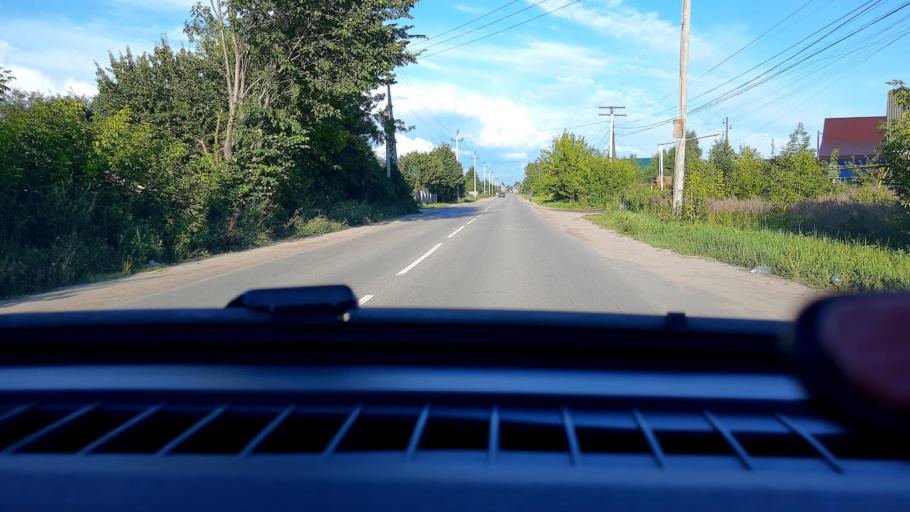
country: RU
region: Nizjnij Novgorod
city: Bor
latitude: 56.3539
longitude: 44.1051
